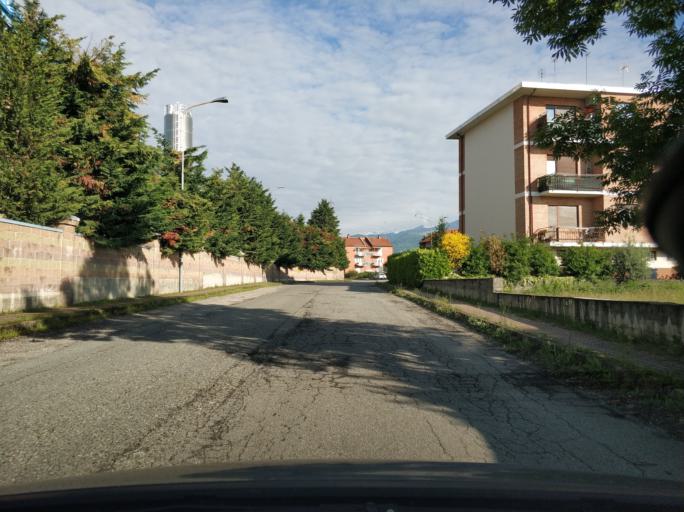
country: IT
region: Piedmont
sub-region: Provincia di Torino
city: Mathi
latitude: 45.2541
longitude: 7.5362
